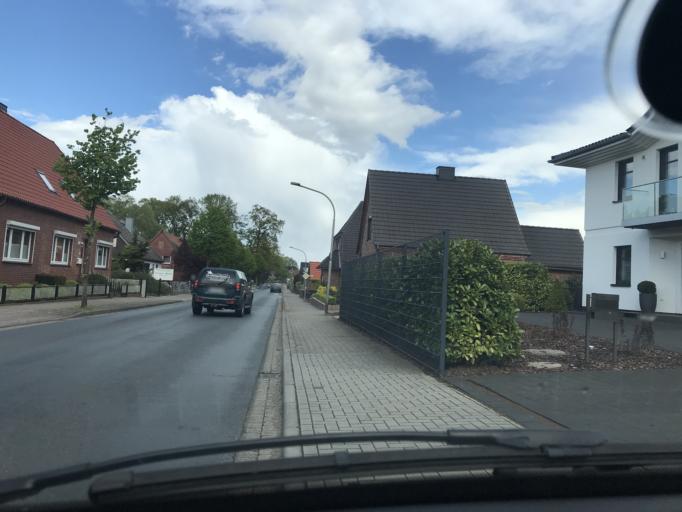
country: DE
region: Lower Saxony
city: Harsefeld
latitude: 53.4608
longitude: 9.5097
